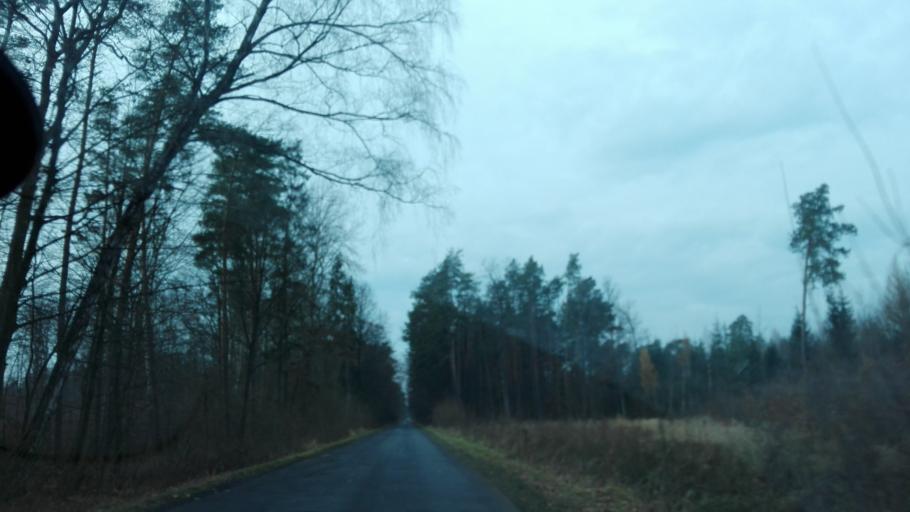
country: PL
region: Lublin Voivodeship
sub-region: Powiat bialski
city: Sosnowka
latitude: 51.7423
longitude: 23.3796
